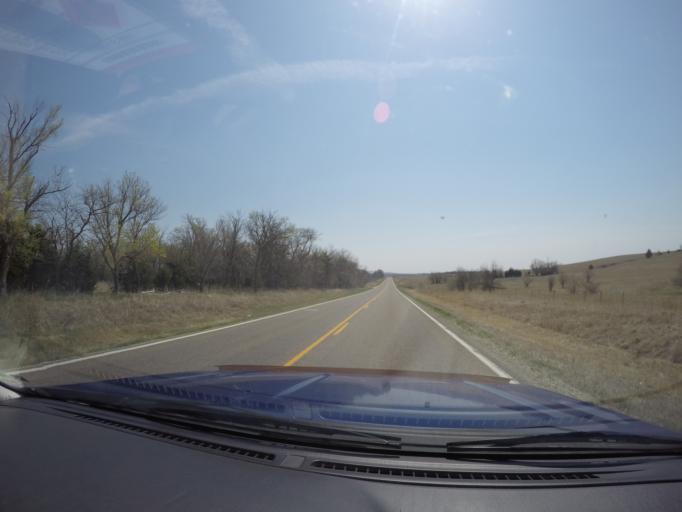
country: US
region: Kansas
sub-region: Morris County
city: Council Grove
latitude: 38.7479
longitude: -96.5012
